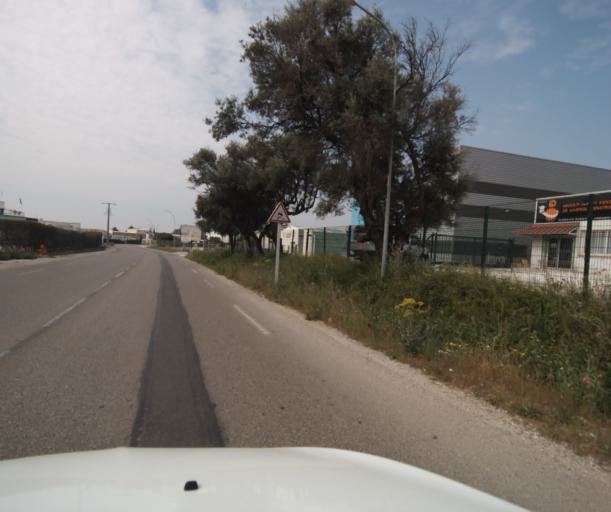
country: FR
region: Provence-Alpes-Cote d'Azur
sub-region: Departement du Var
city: La Farlede
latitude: 43.1485
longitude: 6.0367
